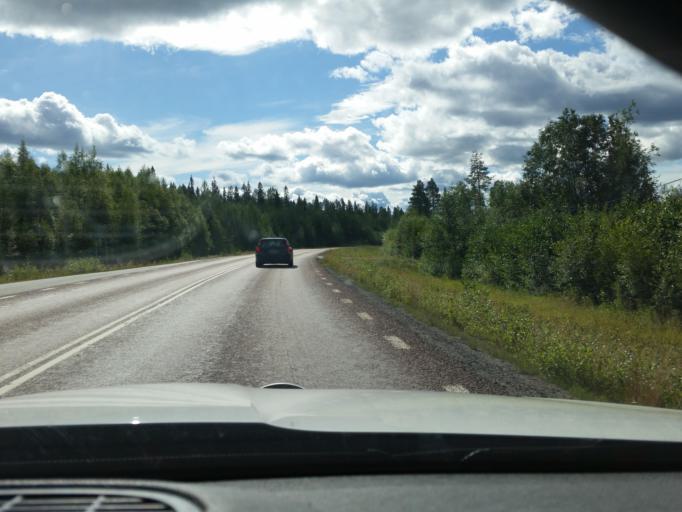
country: SE
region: Norrbotten
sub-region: Alvsbyns Kommun
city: AElvsbyn
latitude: 65.6719
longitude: 21.2165
